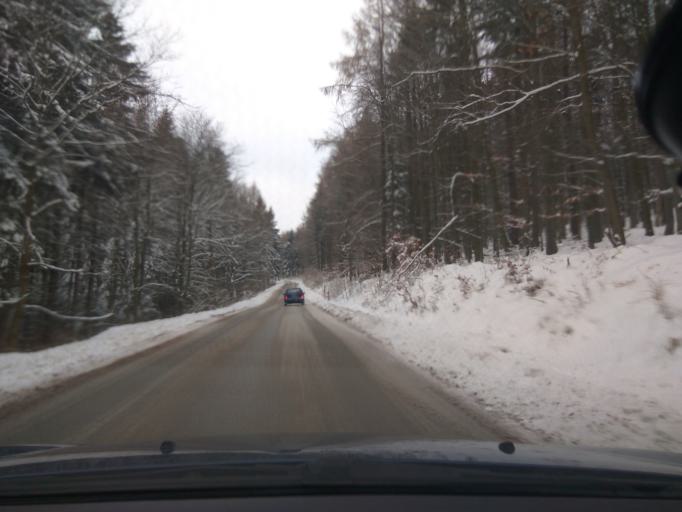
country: CZ
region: Zlin
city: Strani
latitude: 48.8491
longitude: 17.6877
